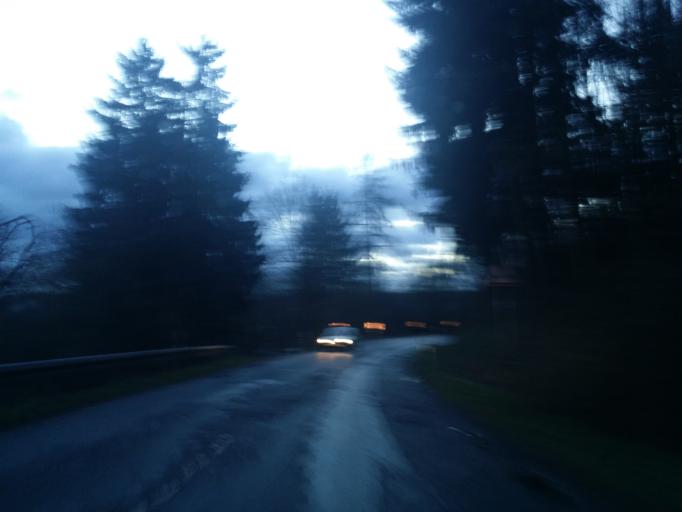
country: DE
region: Hesse
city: Bad Camberg
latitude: 50.2629
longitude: 8.2399
